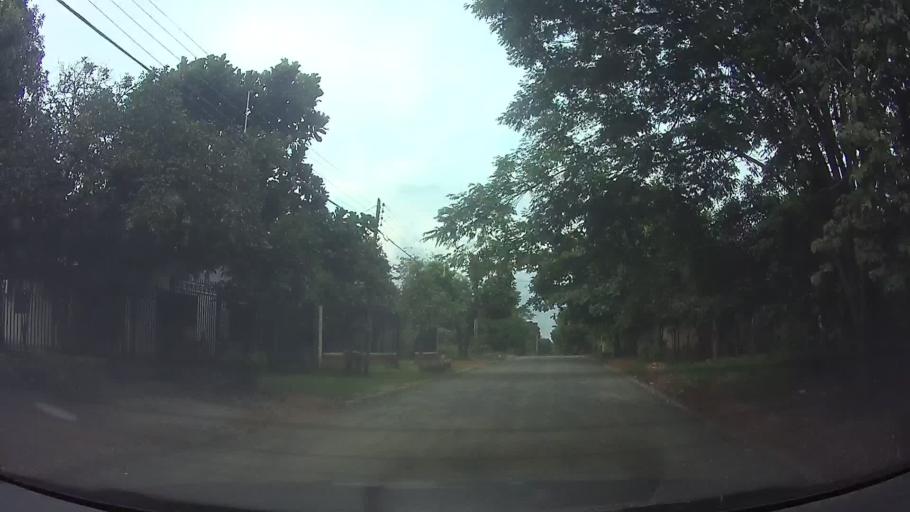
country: PY
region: Central
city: San Lorenzo
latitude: -25.2637
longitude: -57.4618
